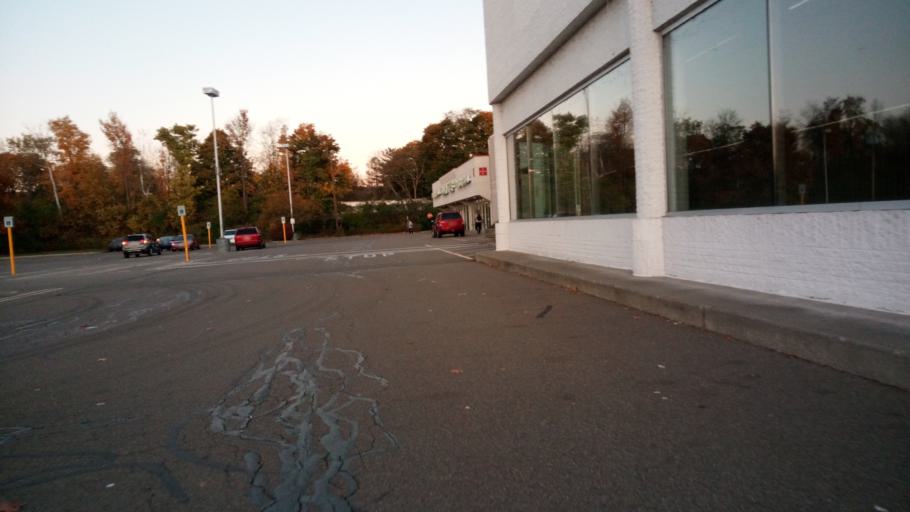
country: US
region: New York
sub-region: Chemung County
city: Elmira
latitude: 42.0827
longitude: -76.8038
